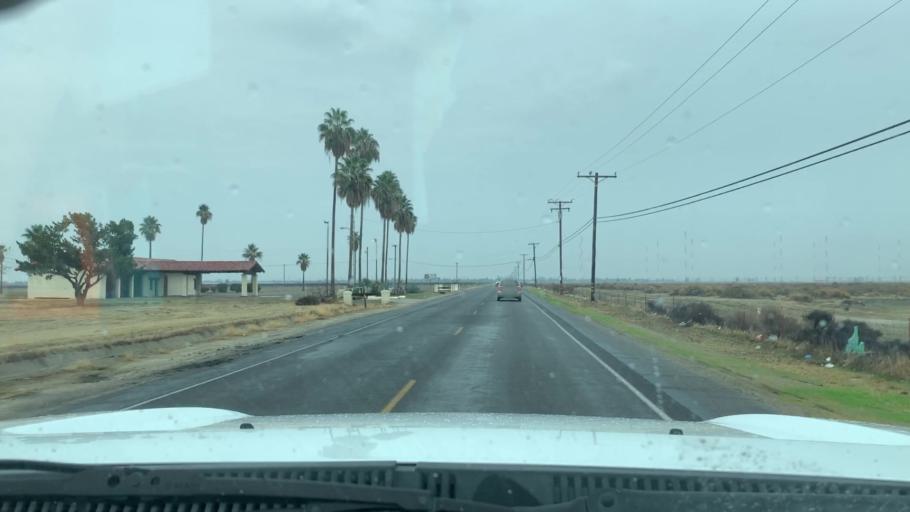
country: US
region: California
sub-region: Kern County
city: Delano
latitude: 35.7613
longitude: -119.2895
